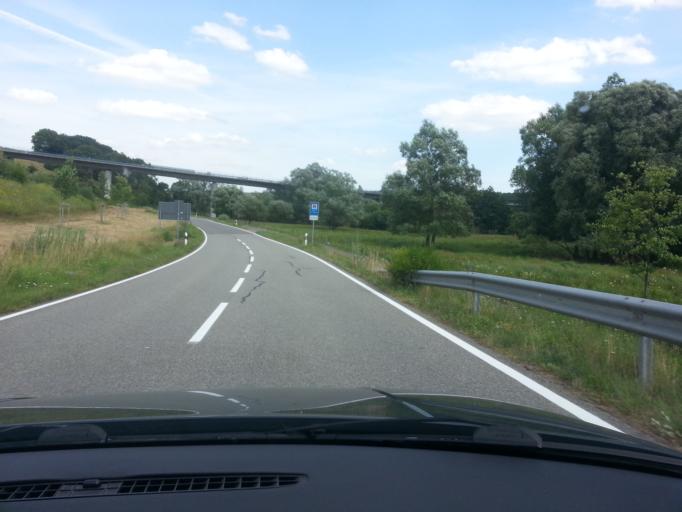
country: DE
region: Rheinland-Pfalz
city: Hornbach
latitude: 49.1862
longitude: 7.3775
